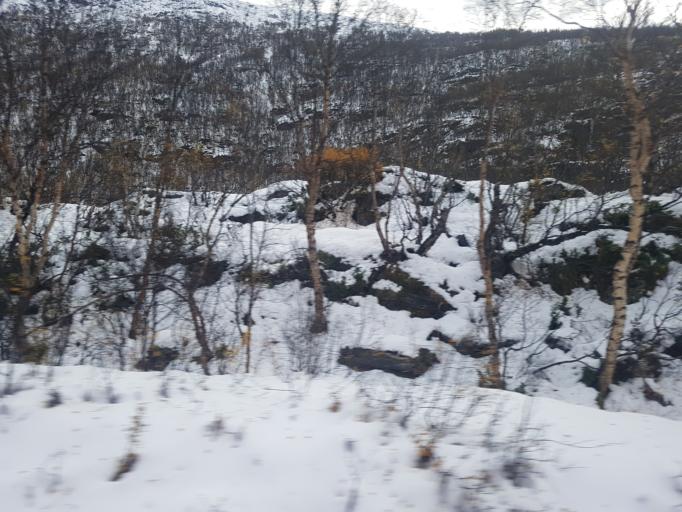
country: NO
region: Sor-Trondelag
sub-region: Oppdal
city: Oppdal
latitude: 62.3391
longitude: 9.6231
